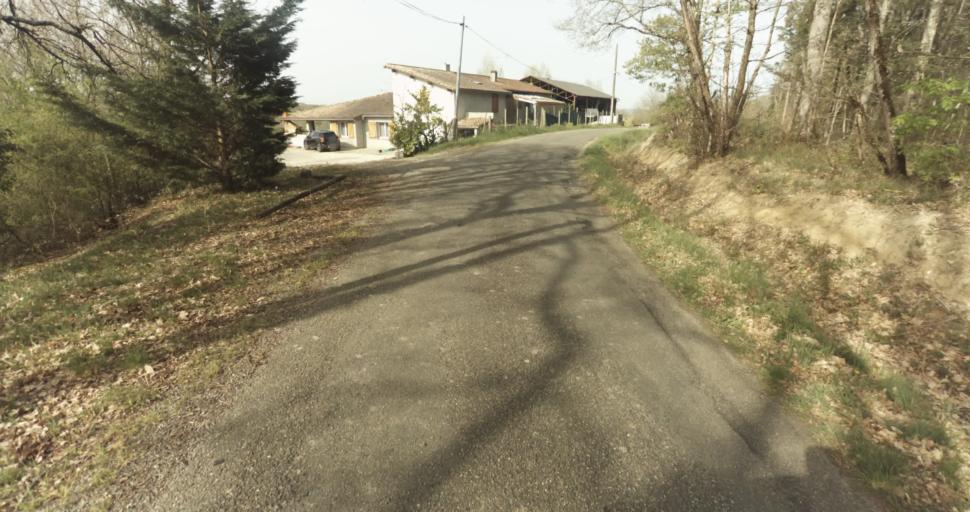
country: FR
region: Midi-Pyrenees
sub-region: Departement du Tarn-et-Garonne
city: Moissac
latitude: 44.1614
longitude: 1.0540
